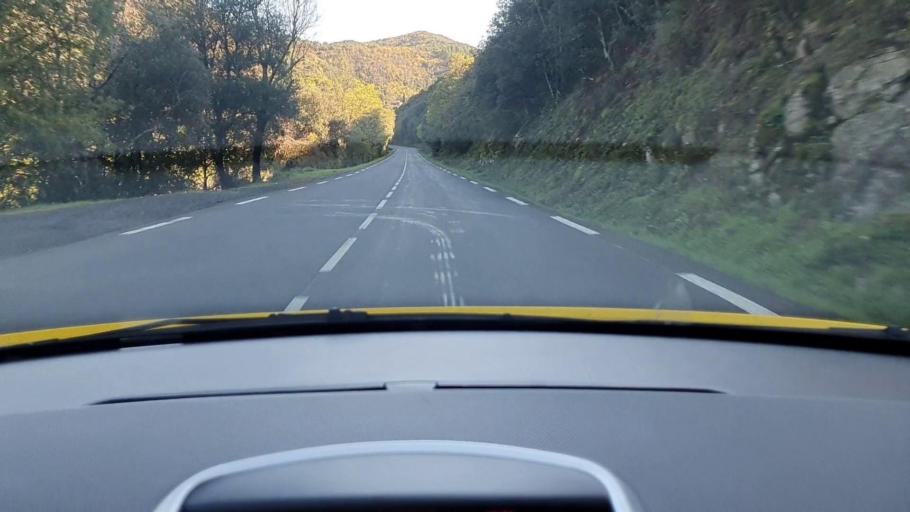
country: FR
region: Languedoc-Roussillon
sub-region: Departement du Gard
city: Sumene
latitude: 44.0307
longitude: 3.6791
